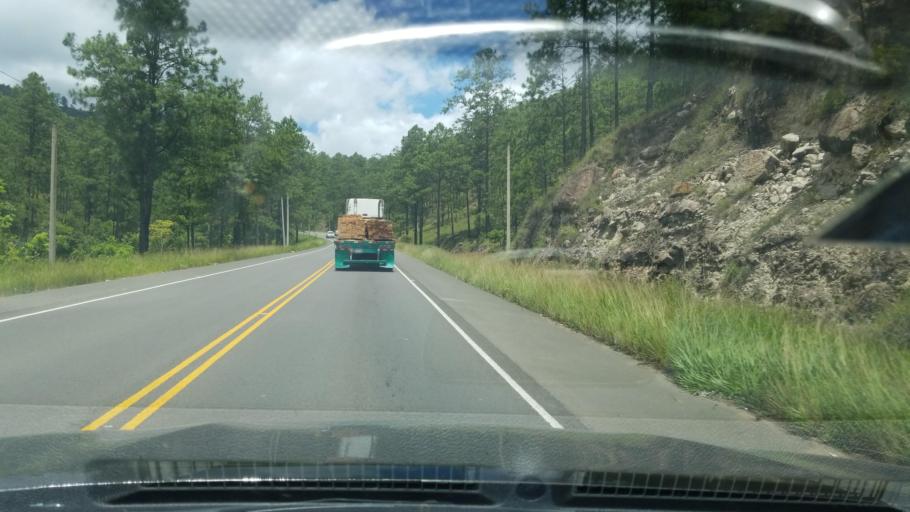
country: HN
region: Francisco Morazan
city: Talanga
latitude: 14.3982
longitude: -87.1263
